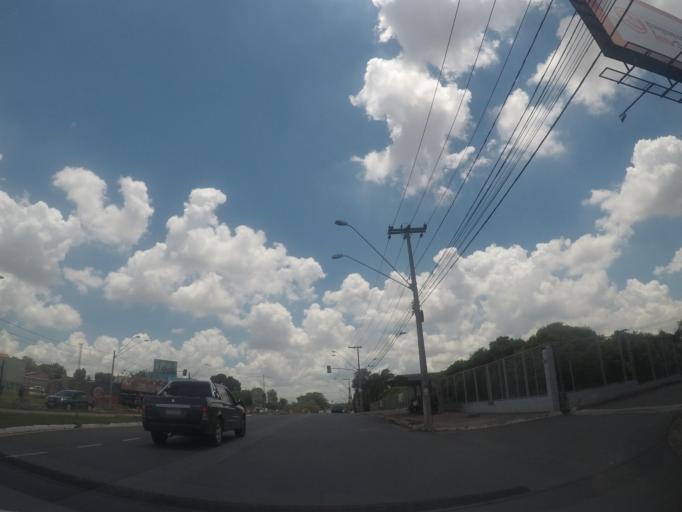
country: BR
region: Sao Paulo
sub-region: Sumare
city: Sumare
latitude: -22.8177
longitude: -47.2469
